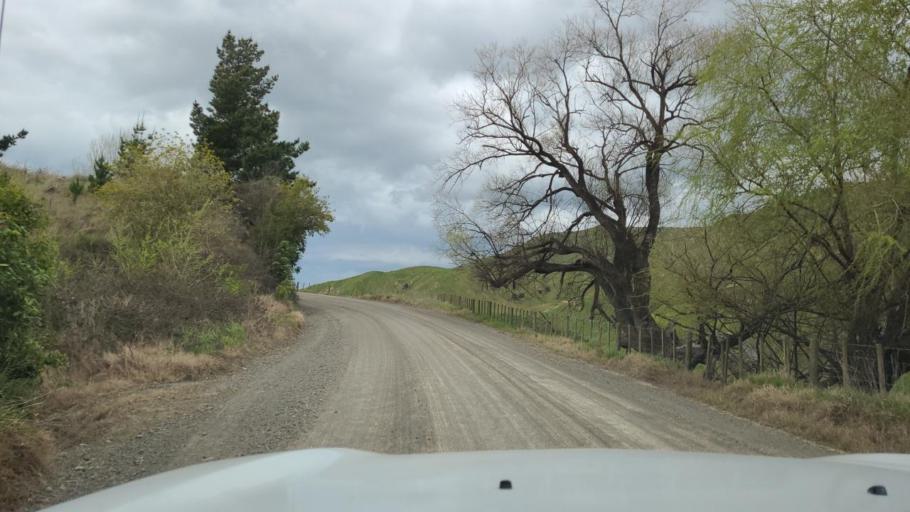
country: NZ
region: Hawke's Bay
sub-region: Napier City
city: Napier
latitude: -39.1865
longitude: 176.9426
